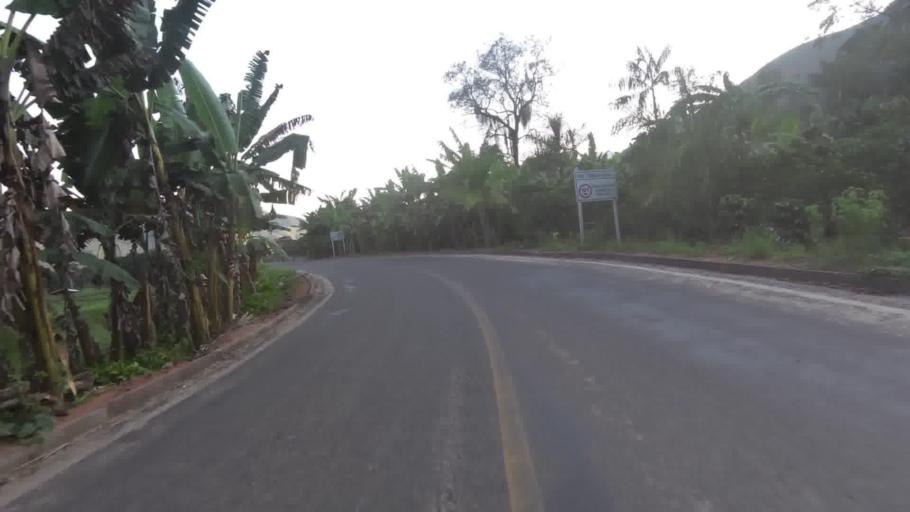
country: BR
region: Espirito Santo
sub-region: Alfredo Chaves
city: Alfredo Chaves
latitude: -20.5843
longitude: -40.6994
